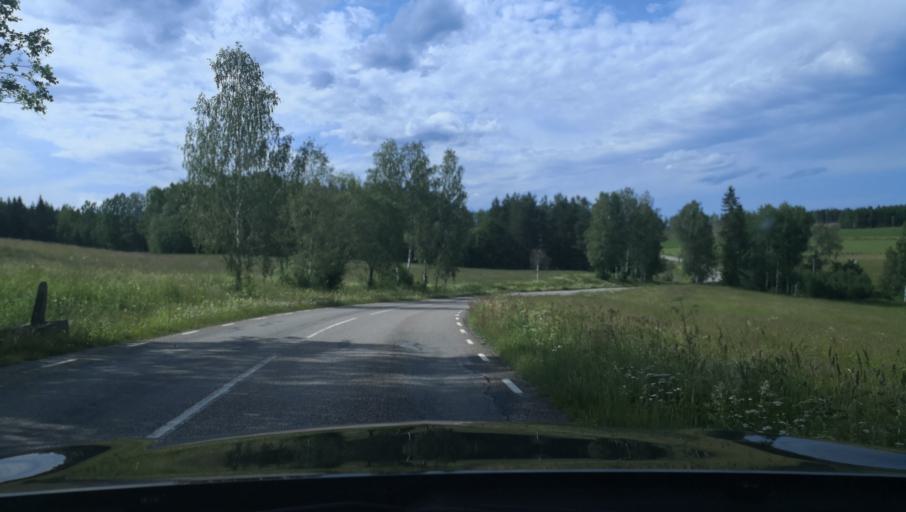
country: SE
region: Dalarna
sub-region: Avesta Kommun
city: Avesta
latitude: 59.9924
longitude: 16.1061
